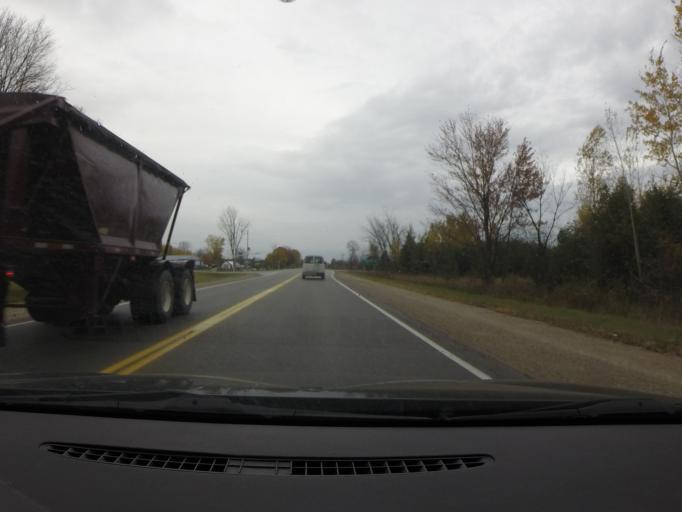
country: CA
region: Ontario
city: Perth
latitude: 44.9714
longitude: -76.2287
